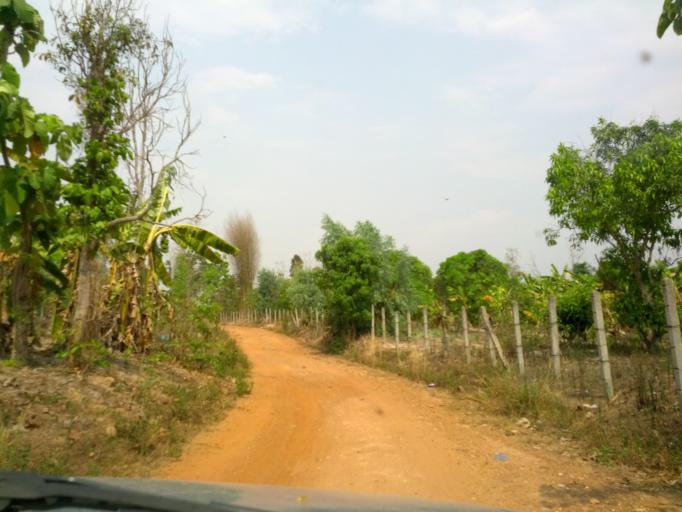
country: TH
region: Chiang Mai
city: Mae Taeng
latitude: 19.1135
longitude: 98.9933
